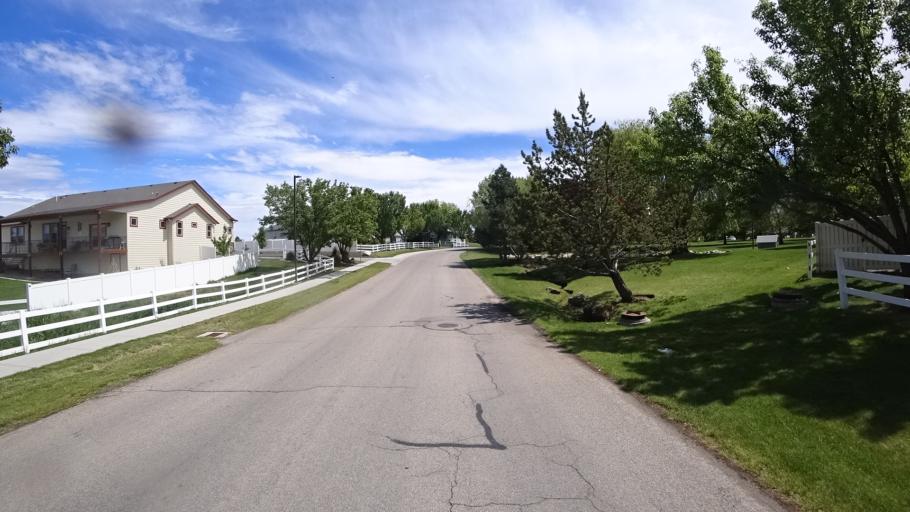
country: US
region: Idaho
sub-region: Ada County
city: Meridian
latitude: 43.5745
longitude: -116.4054
